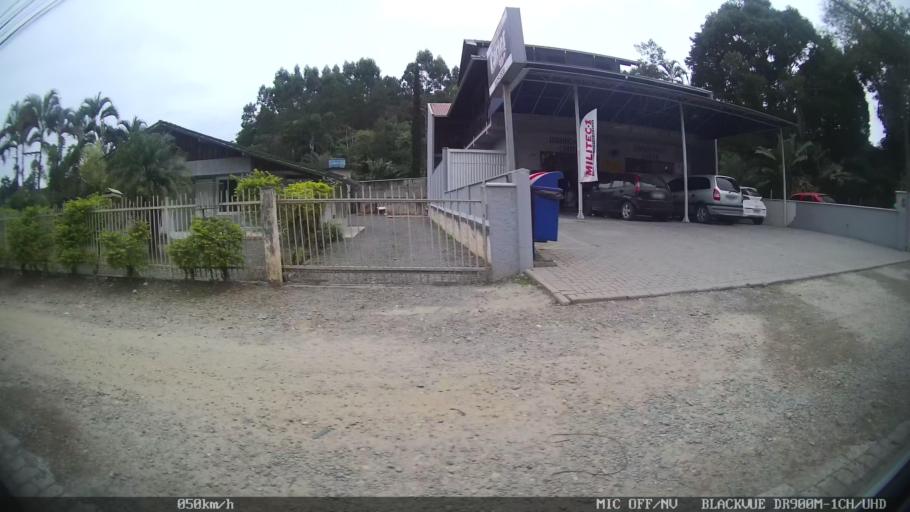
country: BR
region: Santa Catarina
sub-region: Joinville
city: Joinville
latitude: -26.3610
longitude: -48.8422
